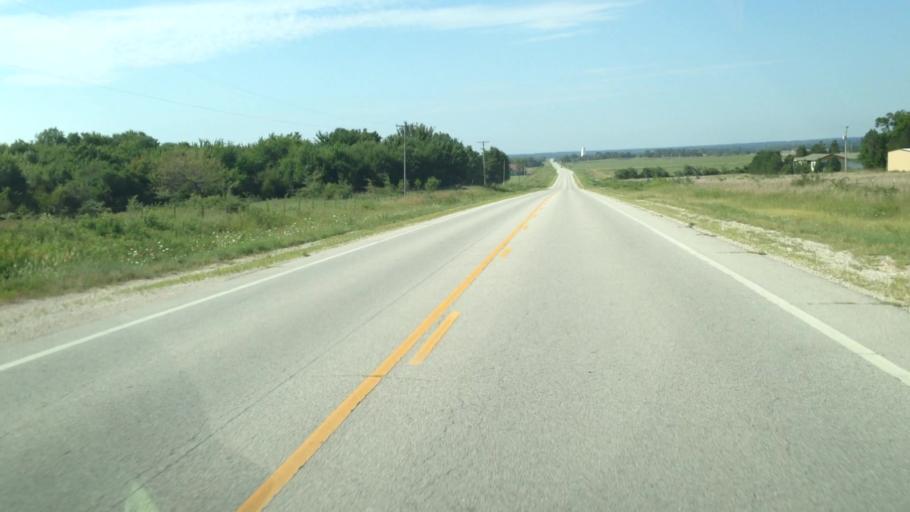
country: US
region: Kansas
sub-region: Neosho County
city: Erie
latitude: 37.4784
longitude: -95.2692
